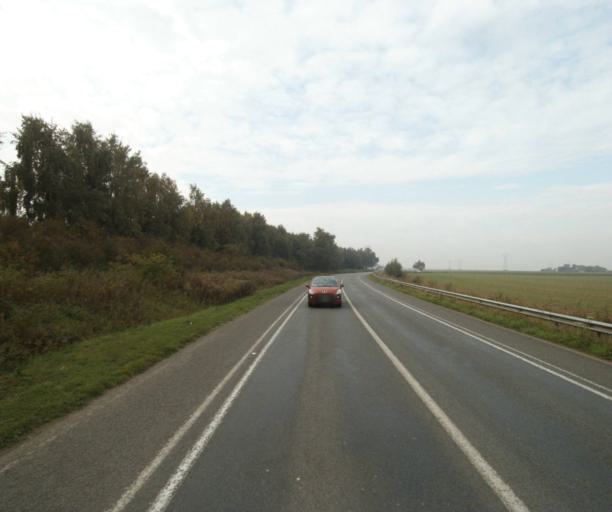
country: FR
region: Nord-Pas-de-Calais
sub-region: Departement du Nord
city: Phalempin
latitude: 50.5288
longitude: 3.0112
